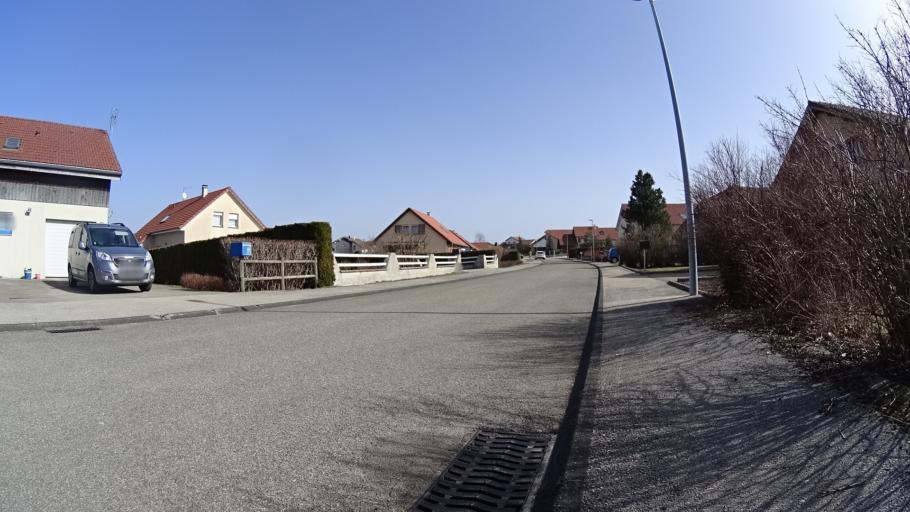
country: FR
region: Franche-Comte
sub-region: Departement du Doubs
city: Frasne
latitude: 46.8511
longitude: 6.1458
